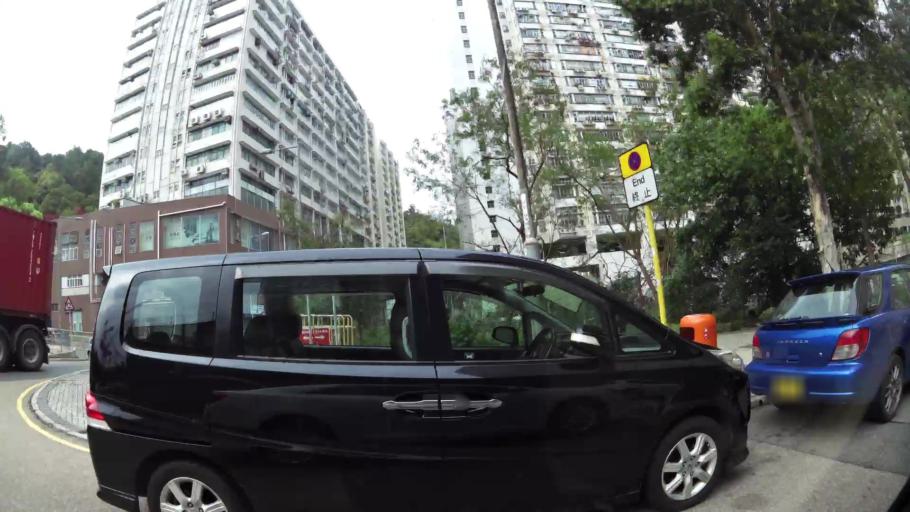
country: HK
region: Sha Tin
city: Sha Tin
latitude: 22.3995
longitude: 114.1913
